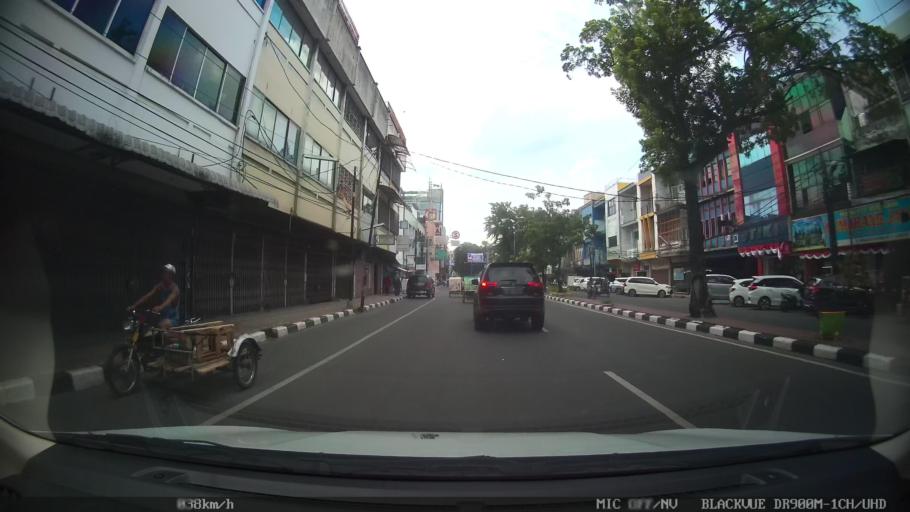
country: ID
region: North Sumatra
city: Medan
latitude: 3.5799
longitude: 98.6834
